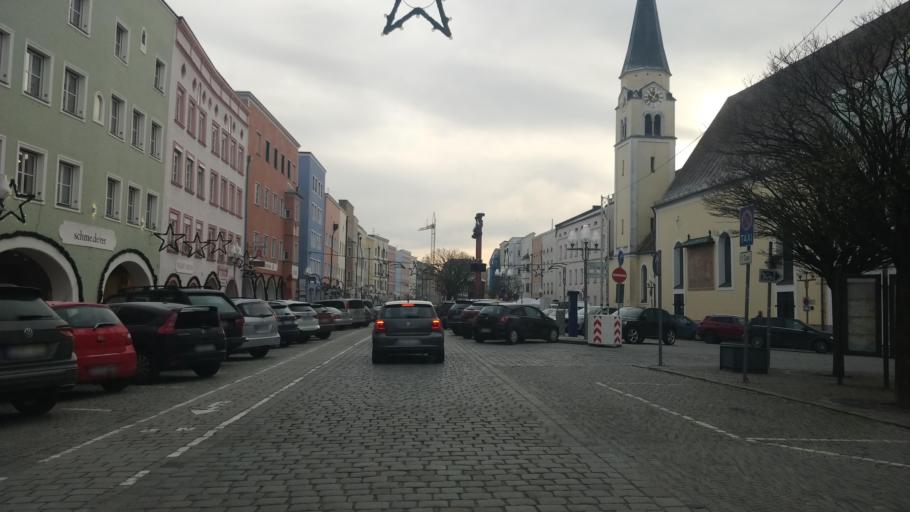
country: DE
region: Bavaria
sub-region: Upper Bavaria
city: Muehldorf
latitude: 48.2415
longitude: 12.5242
